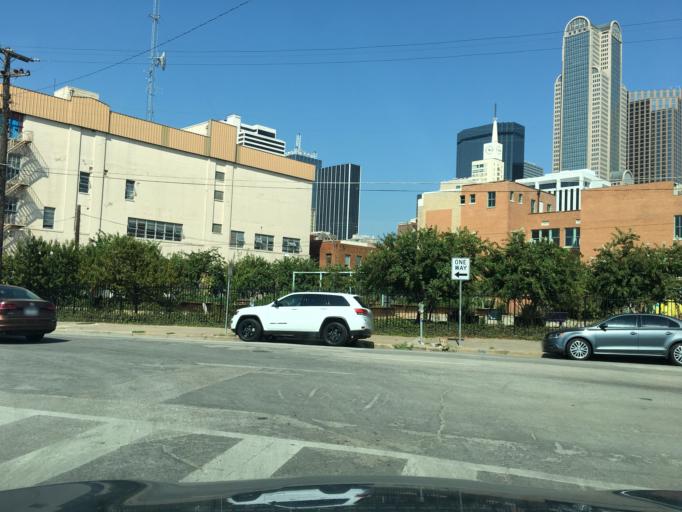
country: US
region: Texas
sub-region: Dallas County
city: Dallas
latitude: 32.7776
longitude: -96.7929
